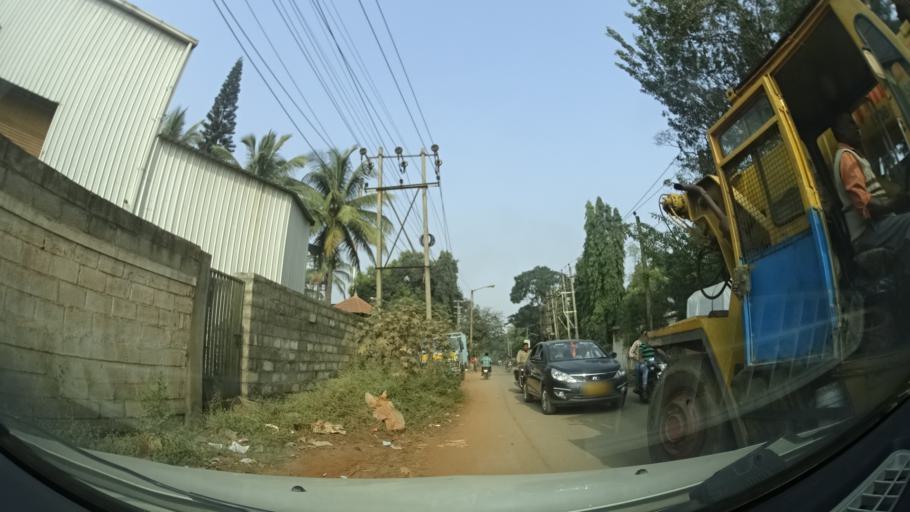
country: IN
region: Karnataka
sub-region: Bangalore Urban
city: Anekal
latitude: 12.8172
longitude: 77.6761
